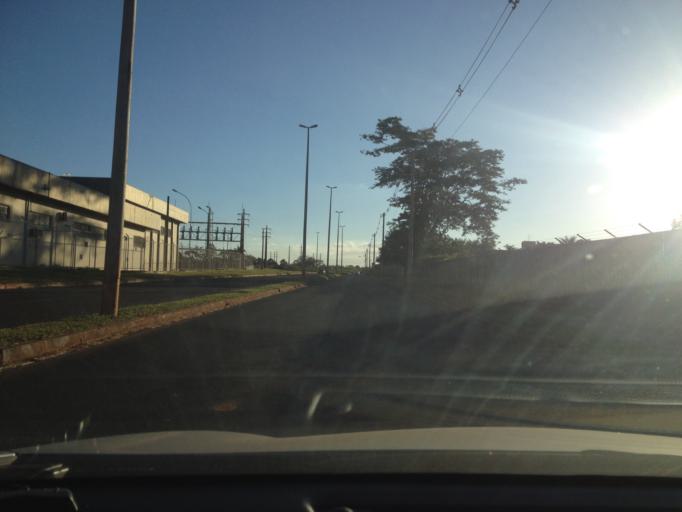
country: BR
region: Federal District
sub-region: Brasilia
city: Brasilia
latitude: -15.7580
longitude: -47.8977
